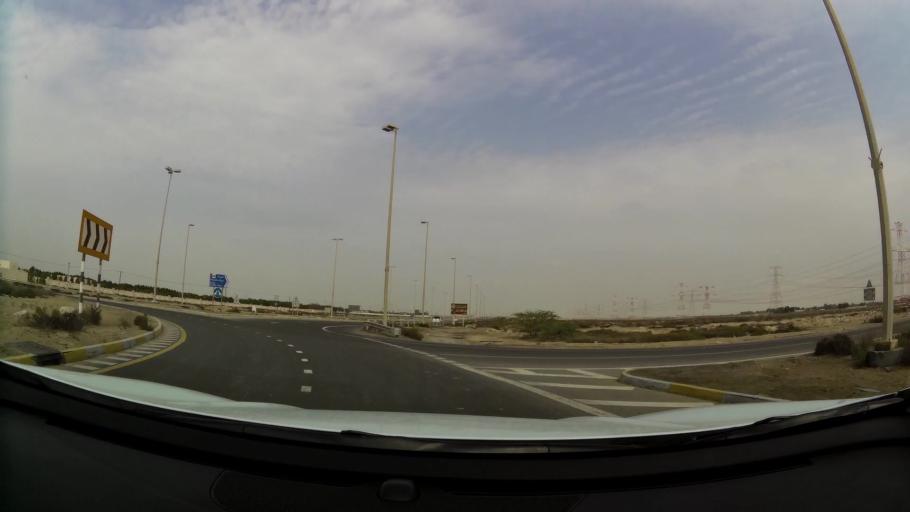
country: AE
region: Abu Dhabi
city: Abu Dhabi
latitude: 24.6653
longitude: 54.7413
